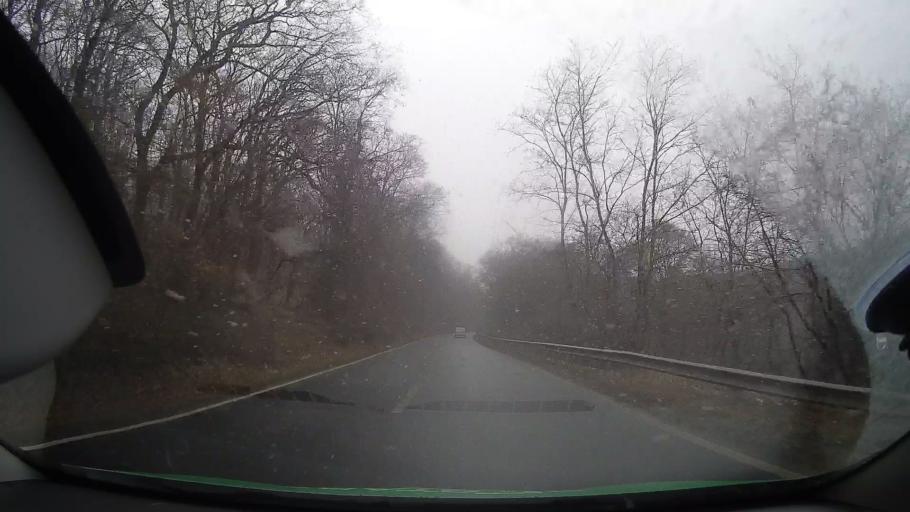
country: RO
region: Sibiu
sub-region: Comuna Blajel
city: Blajel
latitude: 46.1892
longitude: 24.3260
